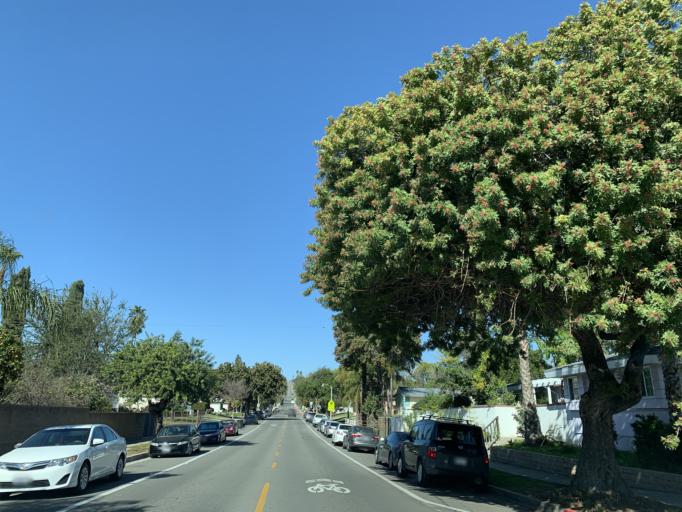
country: US
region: California
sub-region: Orange County
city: Fullerton
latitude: 33.8798
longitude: -117.8984
